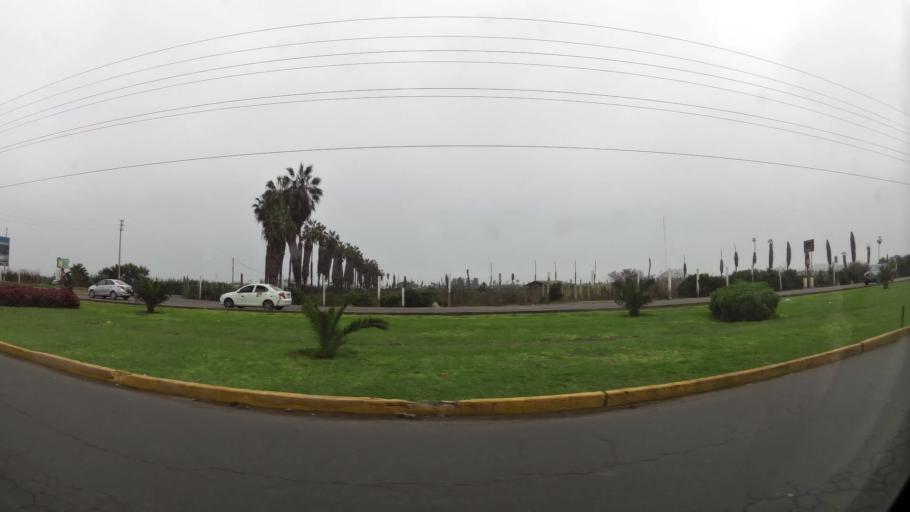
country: PE
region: Lima
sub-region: Lima
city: Surco
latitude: -12.2088
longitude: -76.9879
